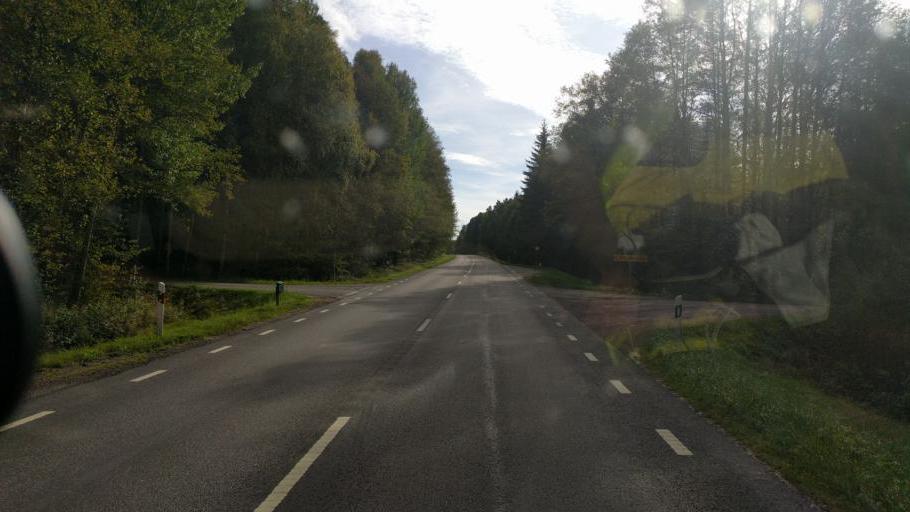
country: SE
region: OEstergoetland
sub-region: Kinda Kommun
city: Kisa
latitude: 57.9415
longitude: 15.6670
